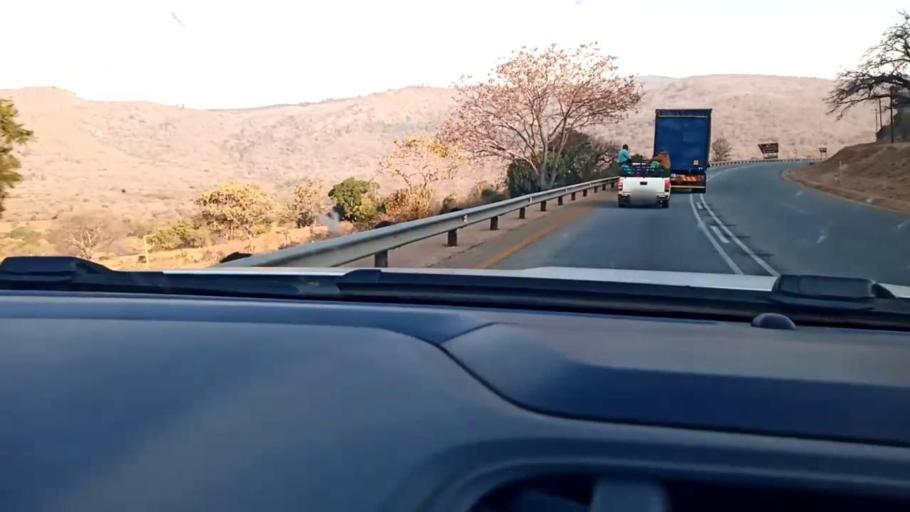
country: ZA
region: Limpopo
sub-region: Mopani District Municipality
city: Ga-Kgapane
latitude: -23.6492
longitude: 30.1718
